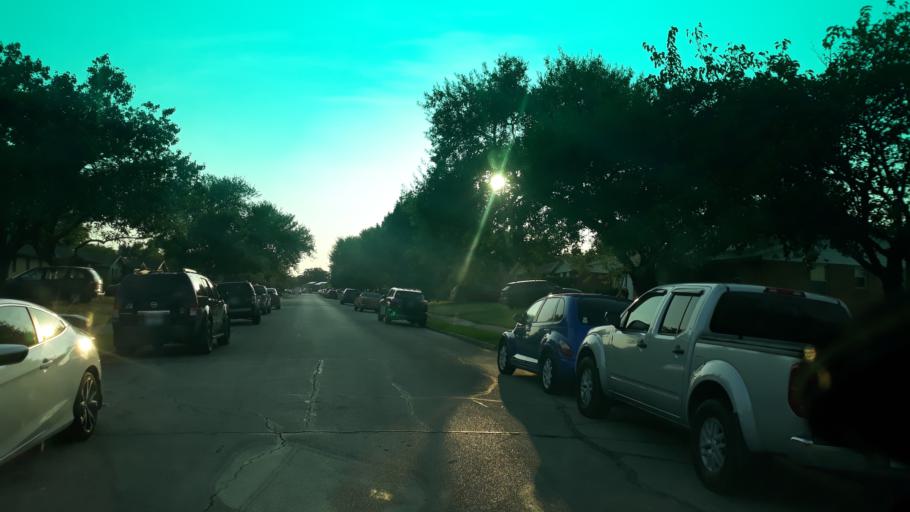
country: US
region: Texas
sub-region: Dallas County
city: Irving
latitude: 32.8437
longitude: -96.9789
